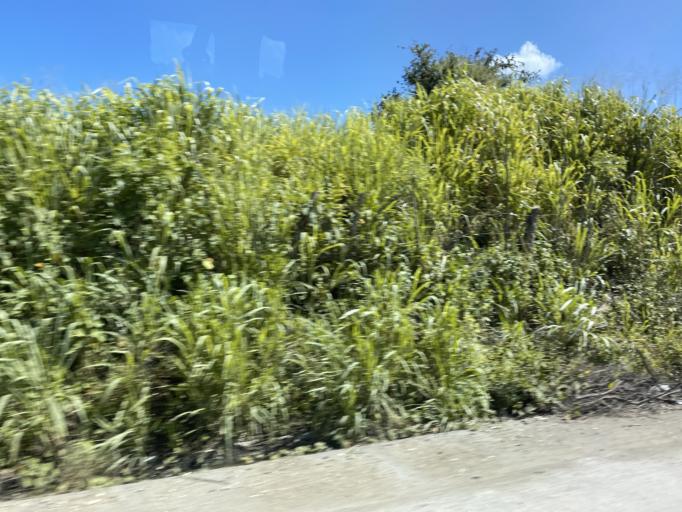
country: DO
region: Puerto Plata
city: Imbert
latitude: 19.8155
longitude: -70.7794
